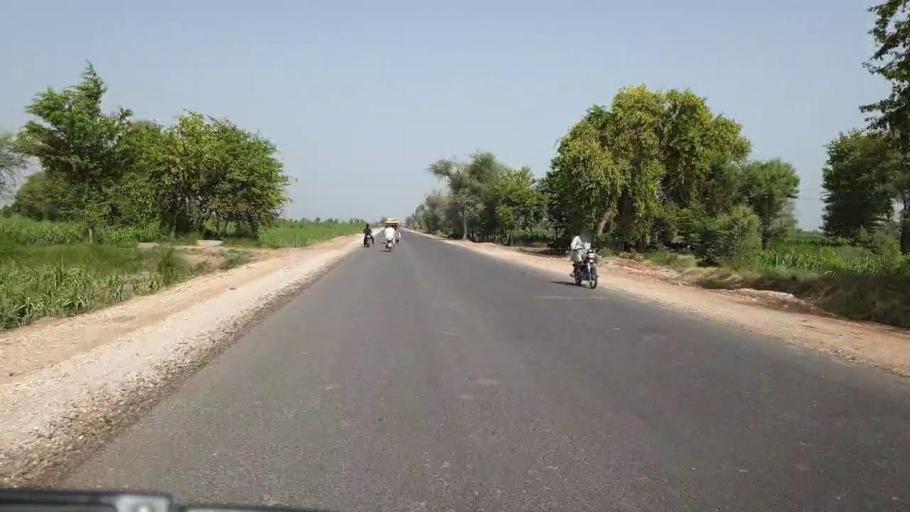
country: PK
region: Sindh
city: Sakrand
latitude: 26.2719
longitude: 68.1591
